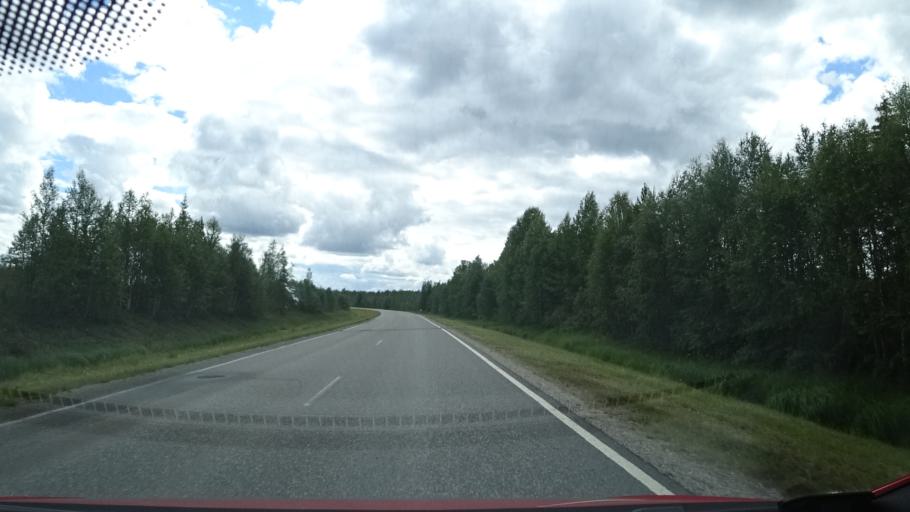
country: FI
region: Lapland
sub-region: Tunturi-Lappi
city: Kittilae
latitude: 67.6208
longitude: 24.9326
